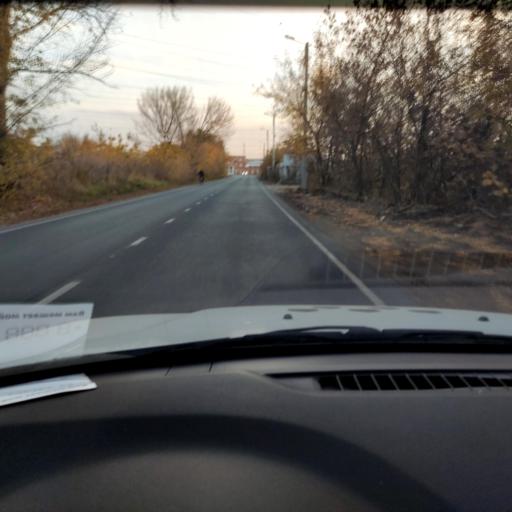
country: RU
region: Samara
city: Zhigulevsk
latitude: 53.5134
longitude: 49.4697
